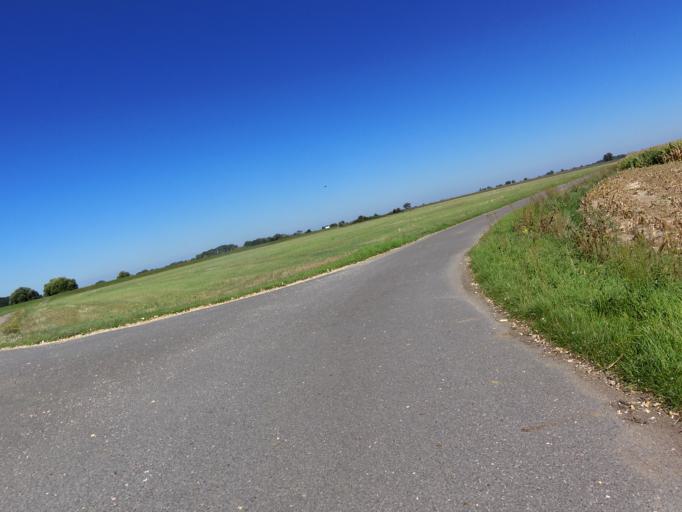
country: DE
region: Saxony-Anhalt
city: Pretzsch
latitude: 51.7262
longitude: 12.8090
